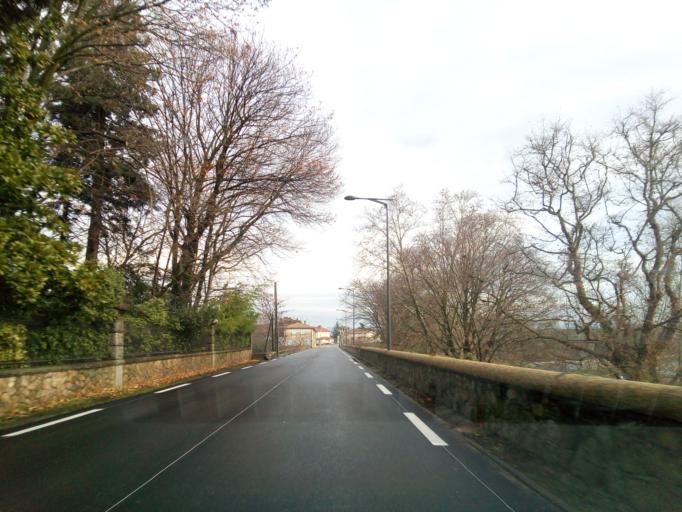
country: FR
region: Rhone-Alpes
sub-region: Departement de l'Ardeche
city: Beauchastel
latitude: 44.8256
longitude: 4.7973
